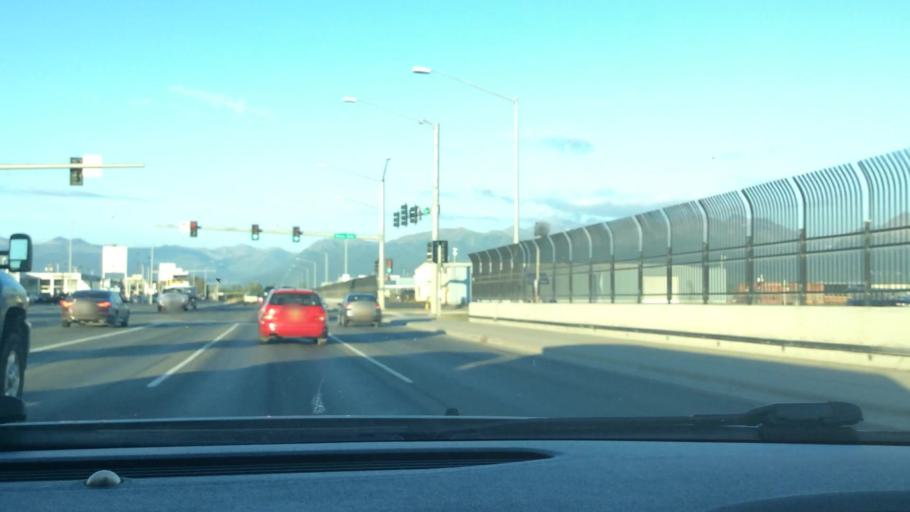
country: US
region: Alaska
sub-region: Anchorage Municipality
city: Anchorage
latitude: 61.2175
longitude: -149.8378
